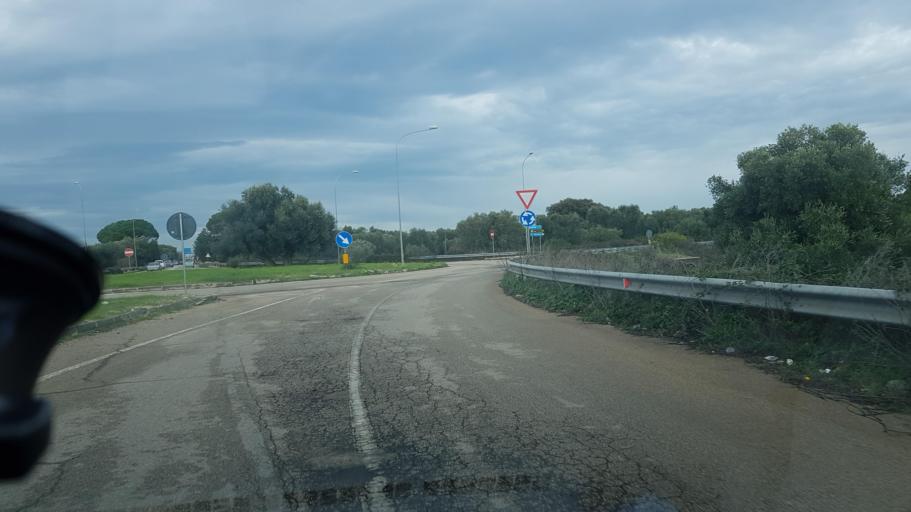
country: IT
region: Apulia
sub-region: Provincia di Brindisi
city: San Vito dei Normanni
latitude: 40.6690
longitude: 17.6957
